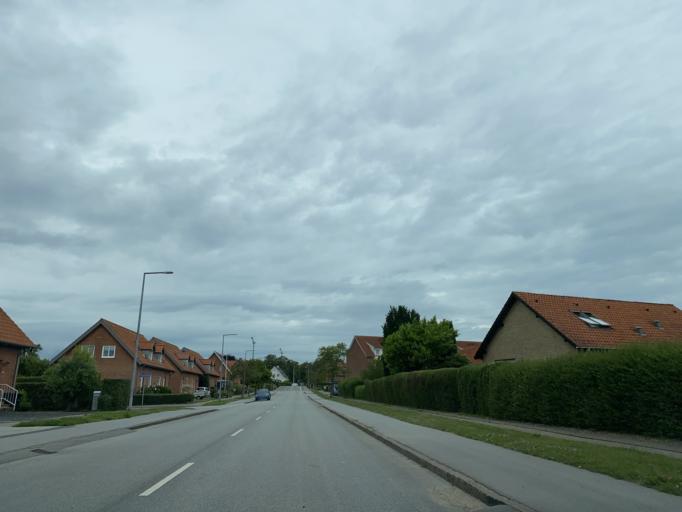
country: DK
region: South Denmark
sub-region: Sonderborg Kommune
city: Sonderborg
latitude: 54.9048
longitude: 9.8047
